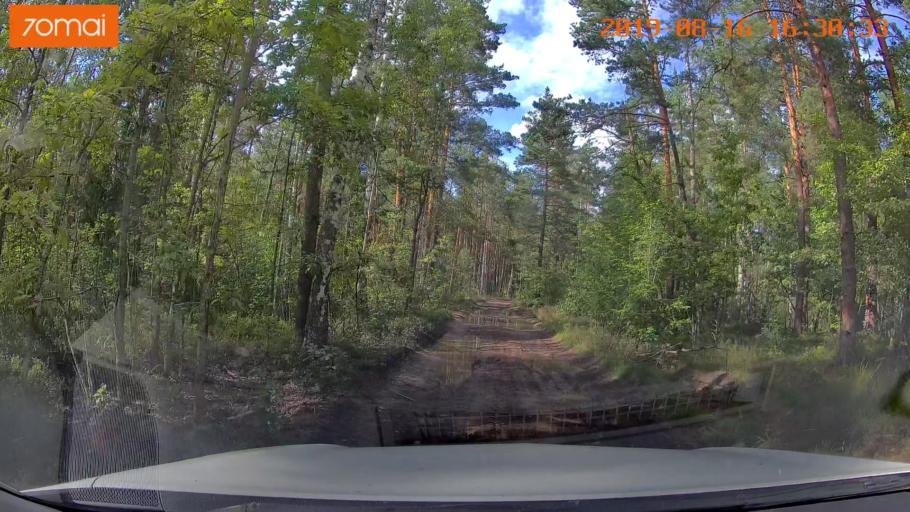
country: BY
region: Mogilev
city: Asipovichy
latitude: 53.2258
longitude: 28.7734
